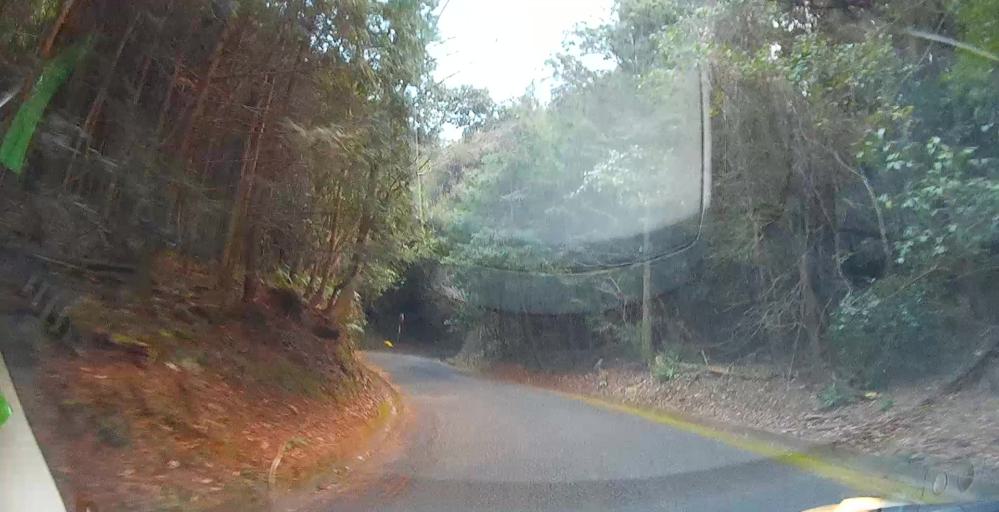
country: JP
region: Kagoshima
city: Izumi
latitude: 32.1178
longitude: 130.4164
